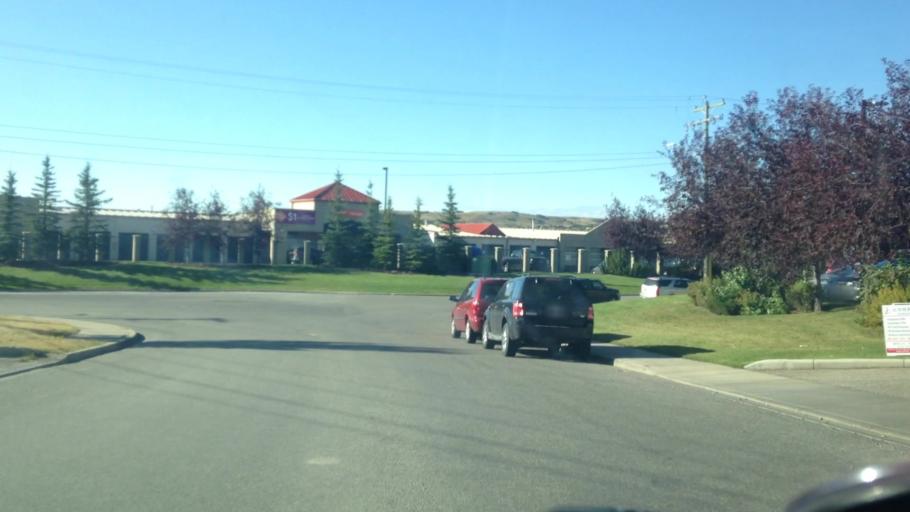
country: CA
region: Alberta
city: Calgary
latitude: 51.1428
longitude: -114.0733
